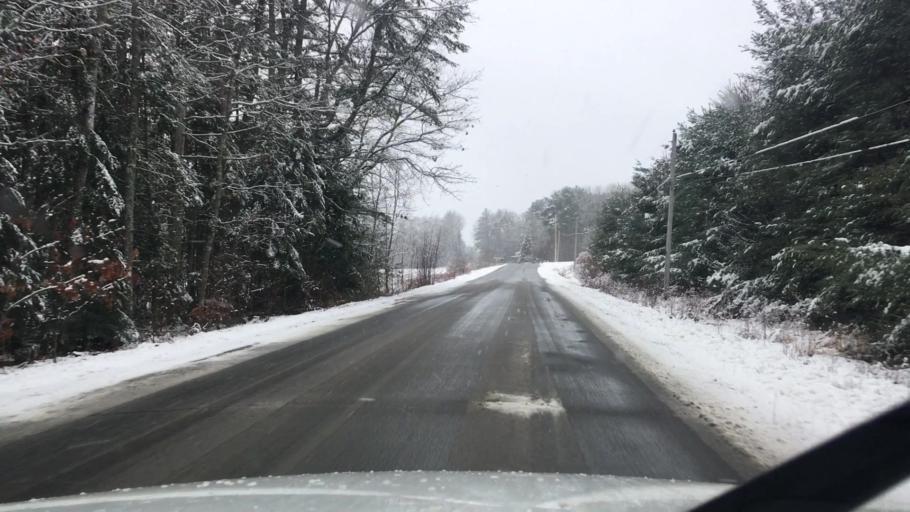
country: US
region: Maine
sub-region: Knox County
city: Union
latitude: 44.1693
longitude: -69.3228
